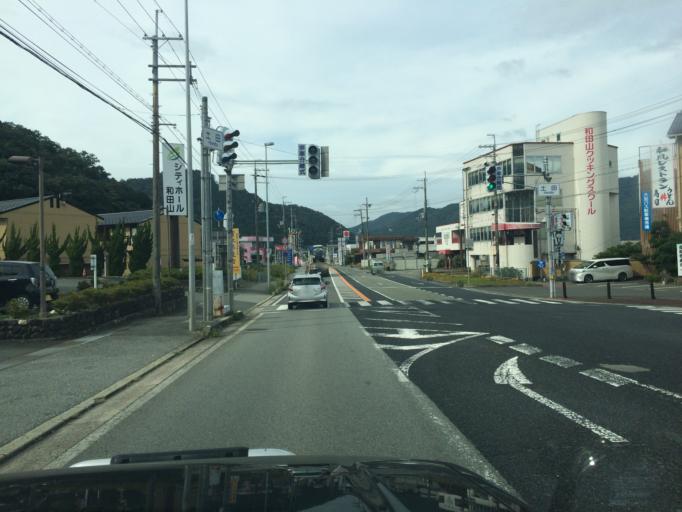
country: JP
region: Hyogo
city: Toyooka
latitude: 35.3434
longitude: 134.8409
